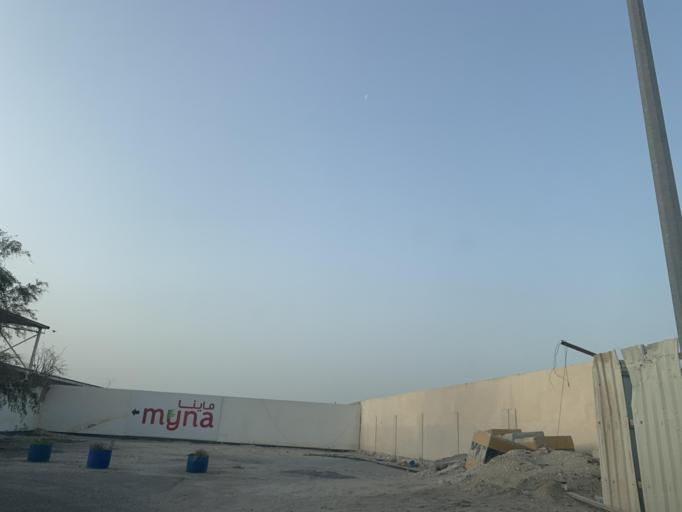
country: BH
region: Manama
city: Manama
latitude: 26.1954
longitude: 50.5939
